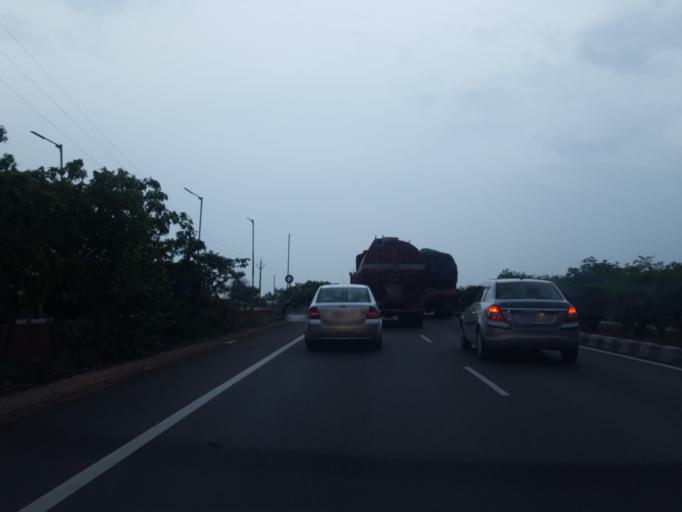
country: IN
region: Telangana
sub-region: Mahbubnagar
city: Farrukhnagar
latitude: 17.1032
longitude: 78.2541
